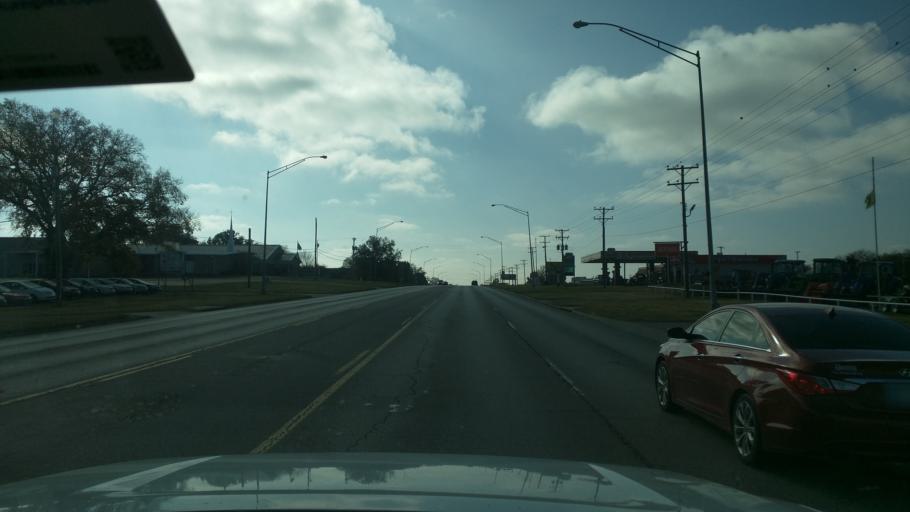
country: US
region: Oklahoma
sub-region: Washington County
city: Dewey
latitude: 36.7677
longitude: -95.9355
